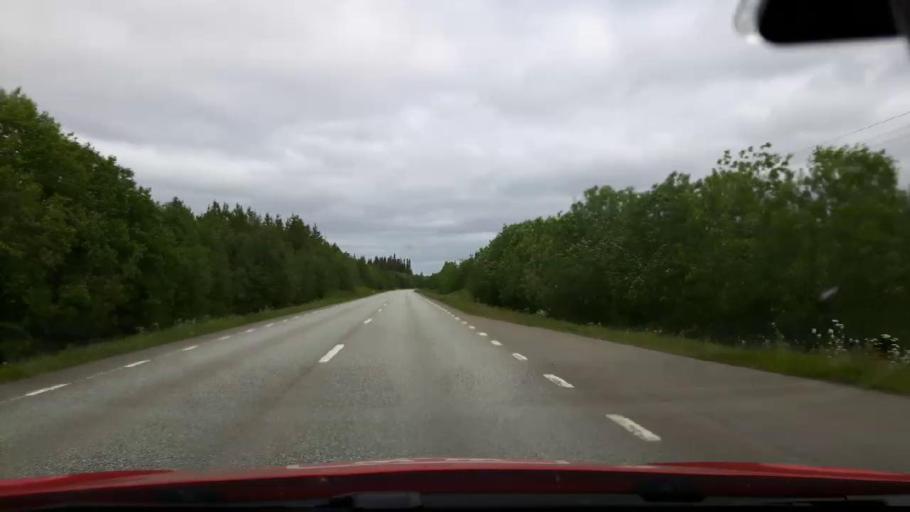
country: SE
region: Jaemtland
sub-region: Krokoms Kommun
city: Krokom
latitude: 63.5609
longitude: 14.6071
